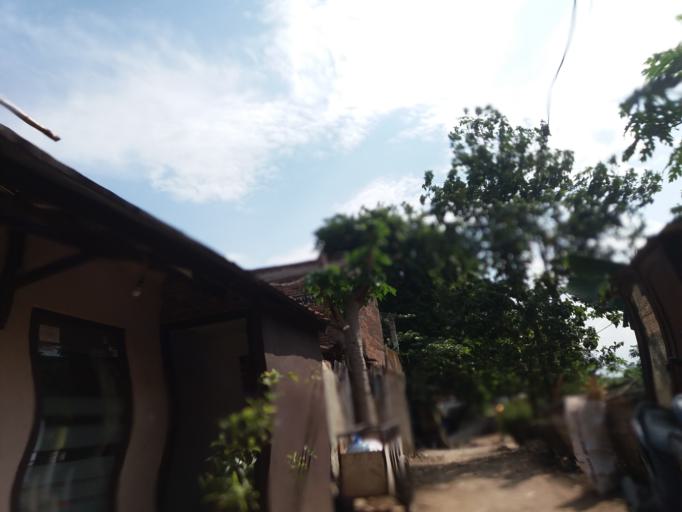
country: ID
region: West Java
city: Bandung
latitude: -6.9206
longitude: 107.6540
